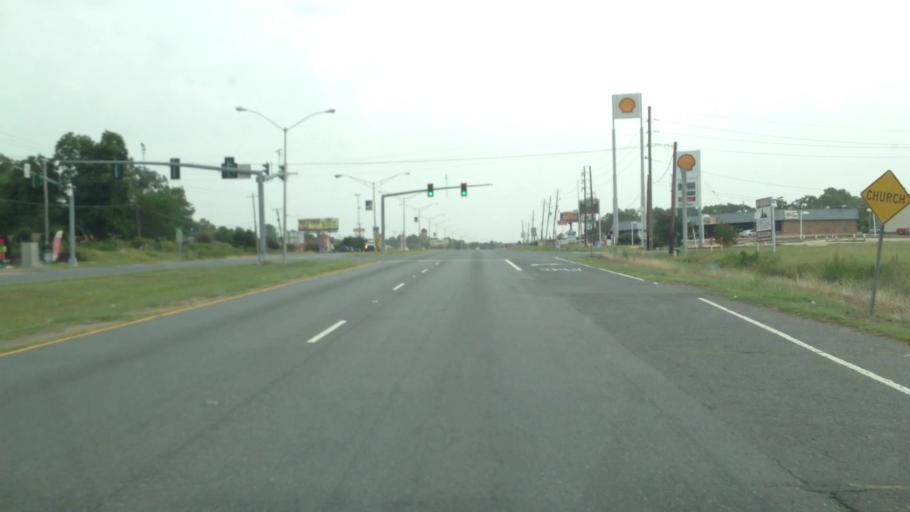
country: US
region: Louisiana
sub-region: De Soto Parish
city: Stonewall
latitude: 32.3908
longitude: -93.8139
